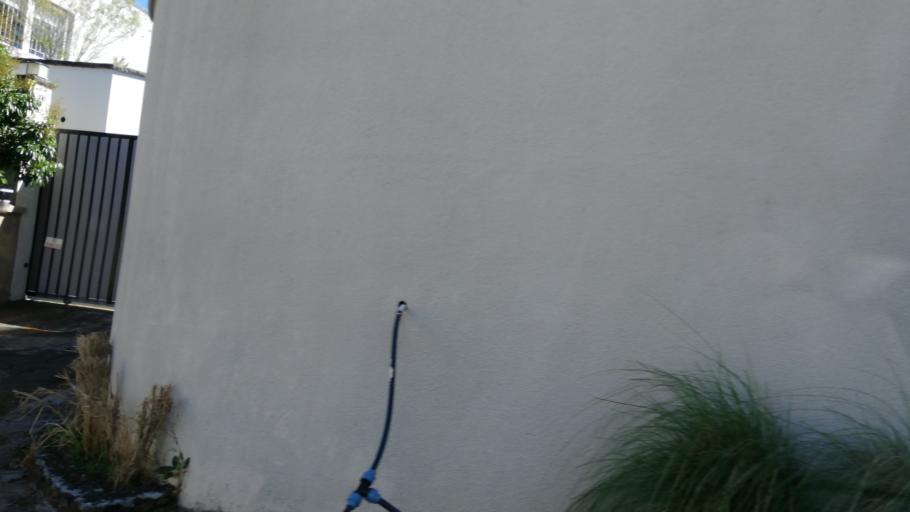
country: MU
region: Plaines Wilhems
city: Ebene
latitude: -20.2321
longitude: 57.4752
